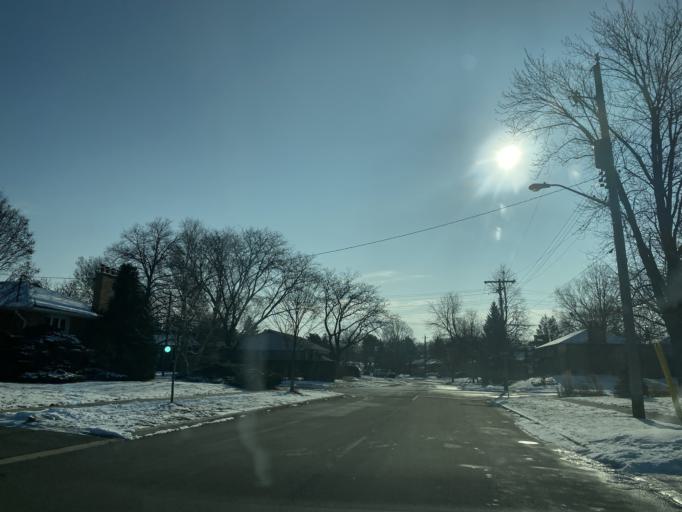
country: CA
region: Ontario
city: Etobicoke
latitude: 43.6709
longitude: -79.5663
